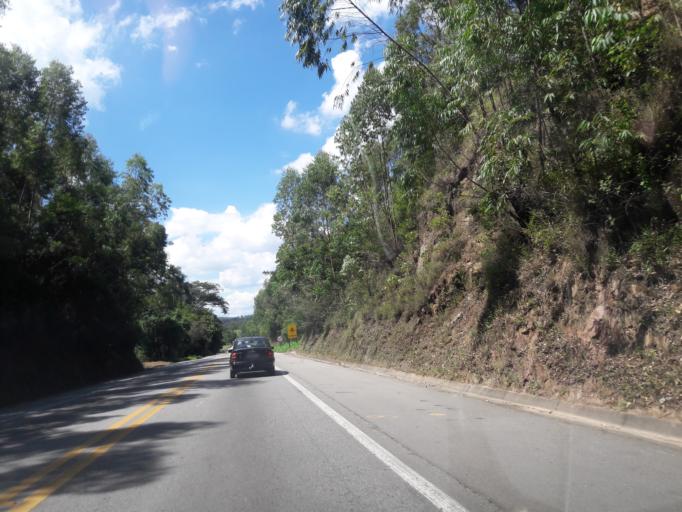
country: BR
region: Sao Paulo
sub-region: Cajamar
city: Cajamar
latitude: -23.3142
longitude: -46.8197
